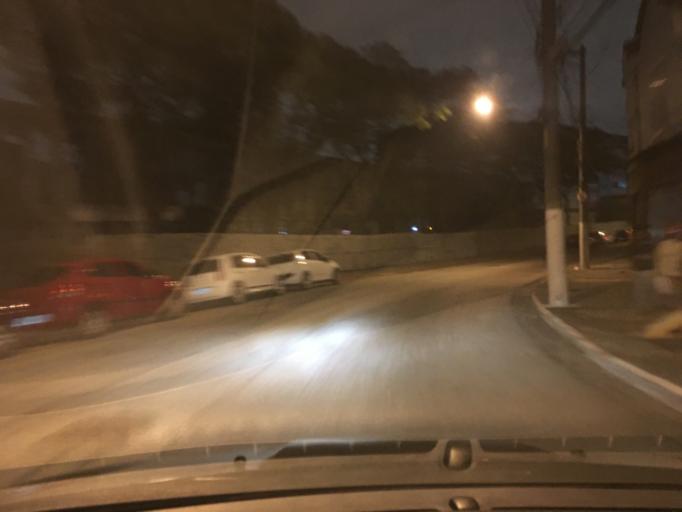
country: BR
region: Sao Paulo
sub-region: Sao Paulo
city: Sao Paulo
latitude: -23.5346
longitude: -46.5846
